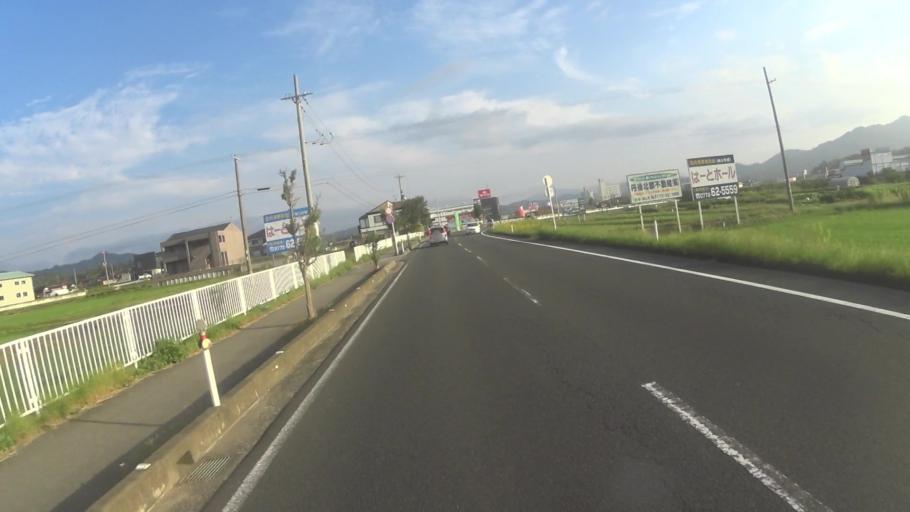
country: JP
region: Kyoto
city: Miyazu
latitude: 35.6125
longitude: 135.0797
